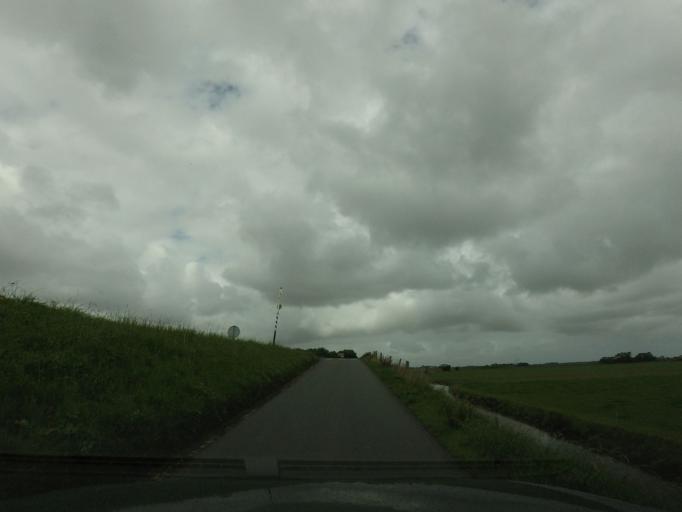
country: NL
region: North Holland
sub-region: Gemeente Schagen
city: Harenkarspel
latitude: 52.7411
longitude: 4.7159
